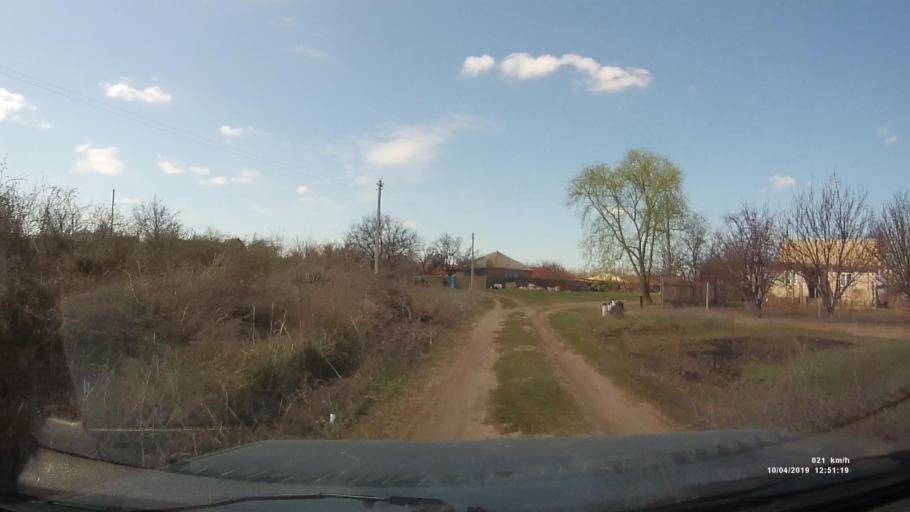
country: RU
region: Rostov
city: Kamensk-Shakhtinskiy
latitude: 48.3591
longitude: 40.2176
